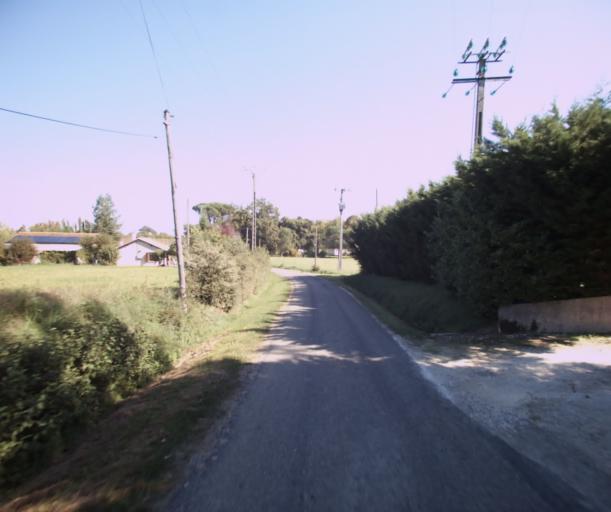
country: FR
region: Midi-Pyrenees
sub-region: Departement du Gers
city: Cazaubon
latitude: 43.9384
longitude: -0.0156
